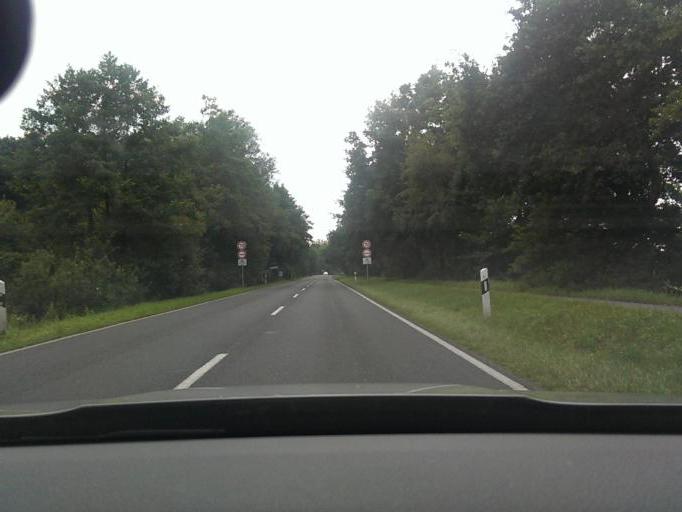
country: DE
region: Lower Saxony
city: Osterholz-Scharmbeck
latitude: 53.1959
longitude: 8.8473
